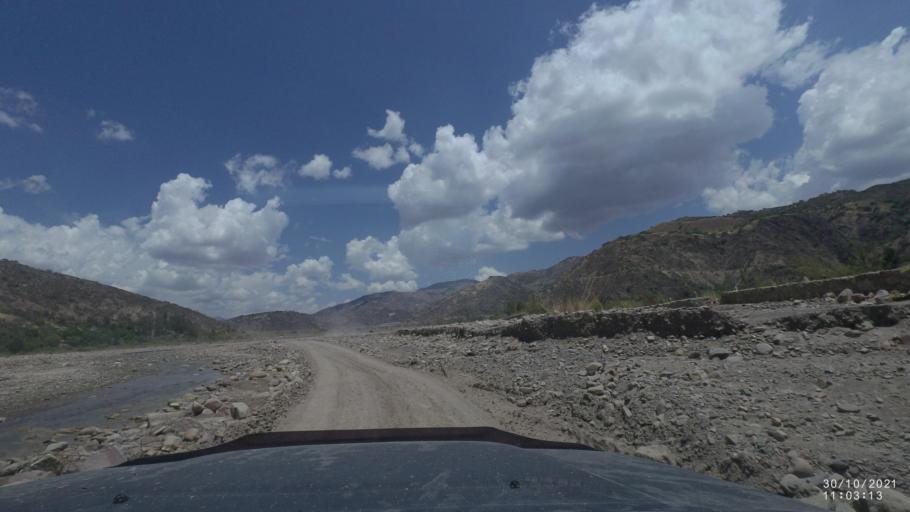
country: BO
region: Cochabamba
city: Sipe Sipe
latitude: -17.5320
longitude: -66.5291
